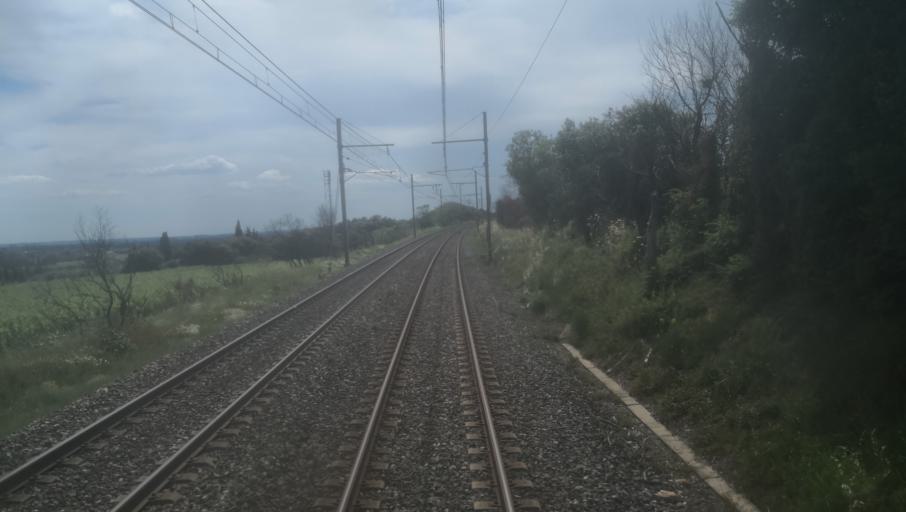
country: FR
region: Languedoc-Roussillon
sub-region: Departement du Gard
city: Jonquieres-Saint-Vincent
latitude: 43.8008
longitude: 4.5871
